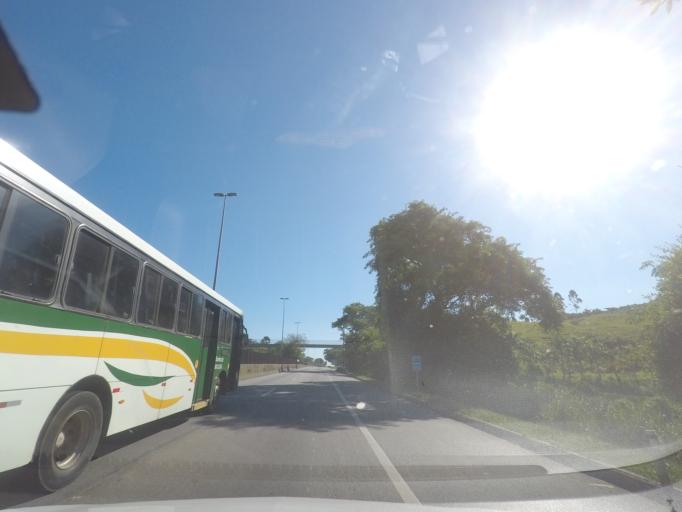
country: BR
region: Rio de Janeiro
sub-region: Guapimirim
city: Guapimirim
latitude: -22.6617
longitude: -43.0935
